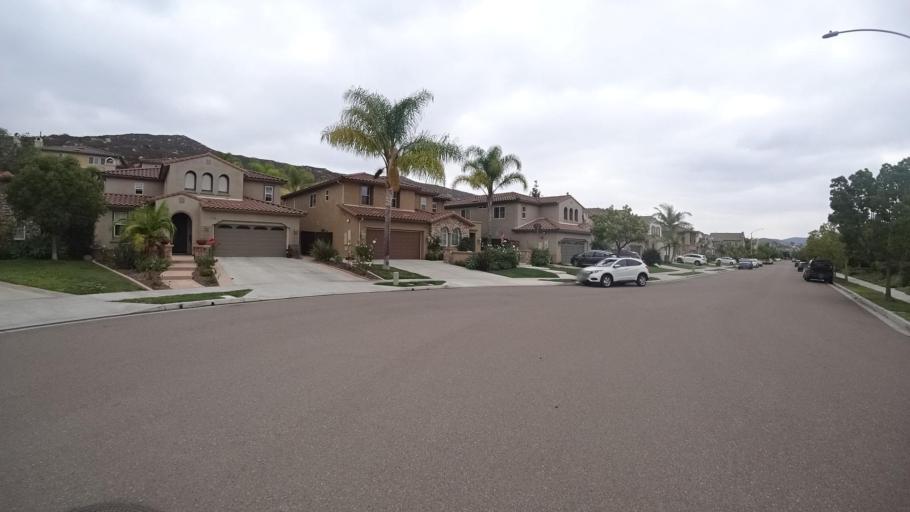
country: US
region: California
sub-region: San Diego County
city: Fairbanks Ranch
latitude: 33.0313
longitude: -117.1102
